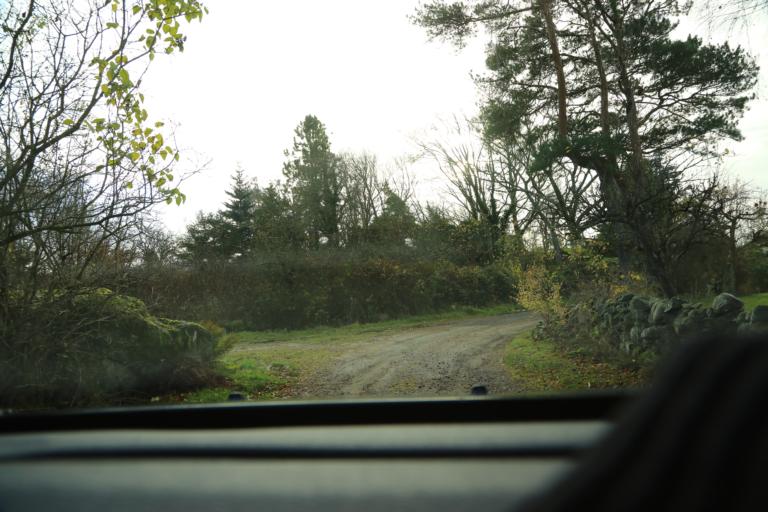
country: SE
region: Halland
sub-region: Varbergs Kommun
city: Varberg
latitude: 57.1697
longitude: 12.2180
